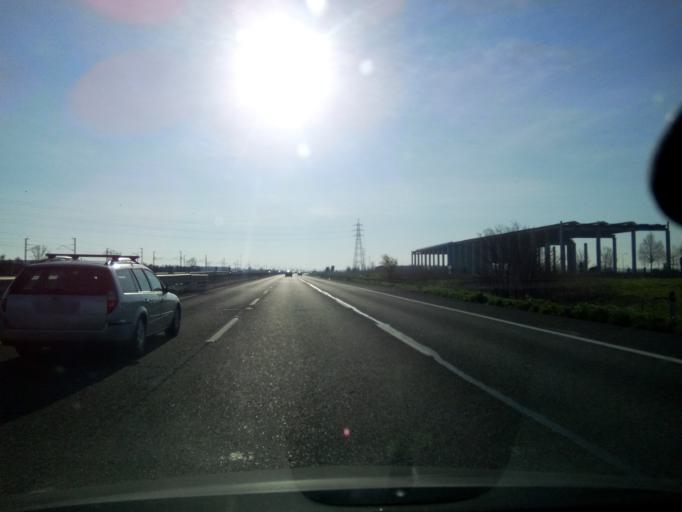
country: IT
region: Emilia-Romagna
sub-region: Provincia di Reggio Emilia
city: Massenzatico
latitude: 44.7110
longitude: 10.7166
